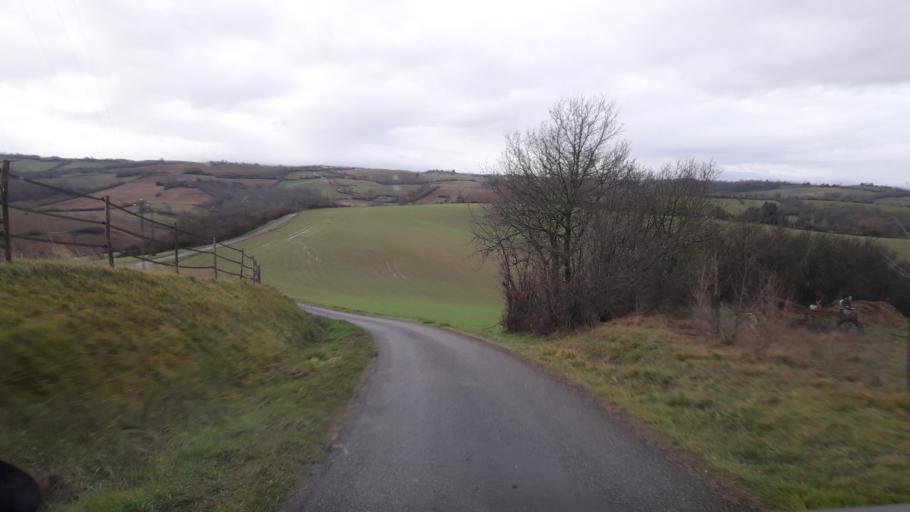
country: FR
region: Midi-Pyrenees
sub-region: Departement de la Haute-Garonne
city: Carbonne
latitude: 43.2574
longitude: 1.2583
